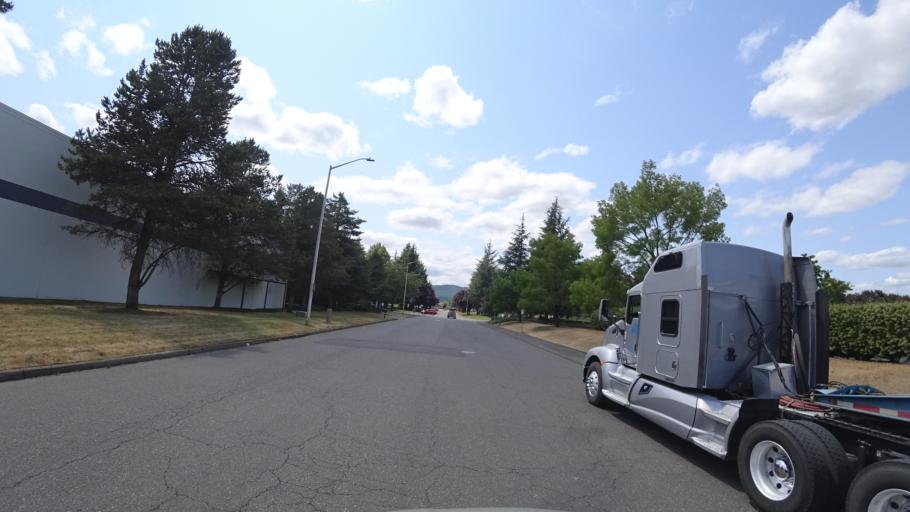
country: US
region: Oregon
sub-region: Washington County
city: West Haven
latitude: 45.6203
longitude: -122.7703
